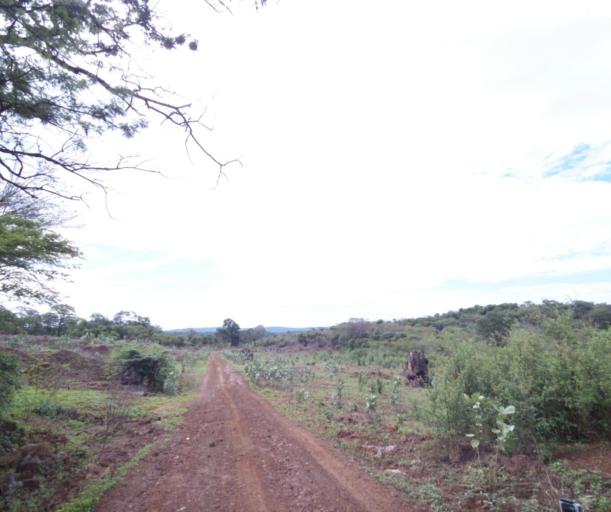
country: BR
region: Bahia
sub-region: Carinhanha
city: Carinhanha
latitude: -14.2334
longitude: -44.4270
